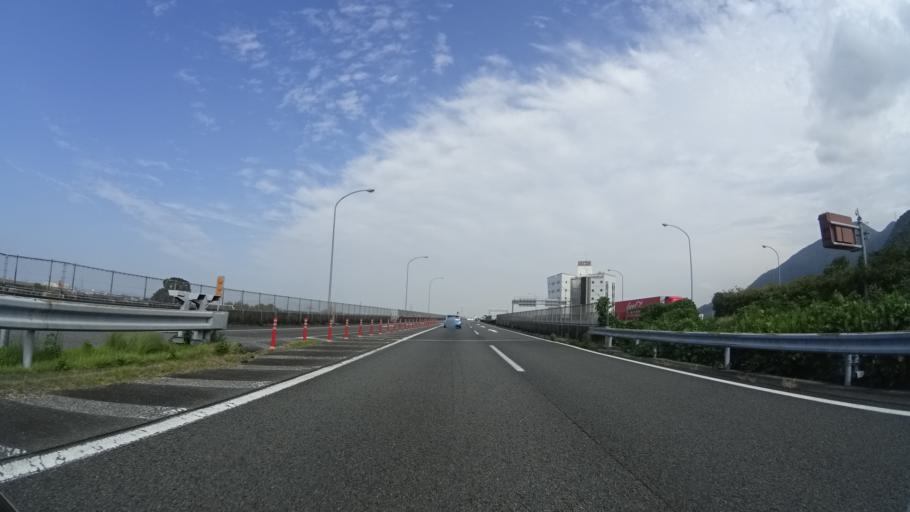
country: JP
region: Kumamoto
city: Yatsushiro
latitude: 32.5045
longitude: 130.6461
